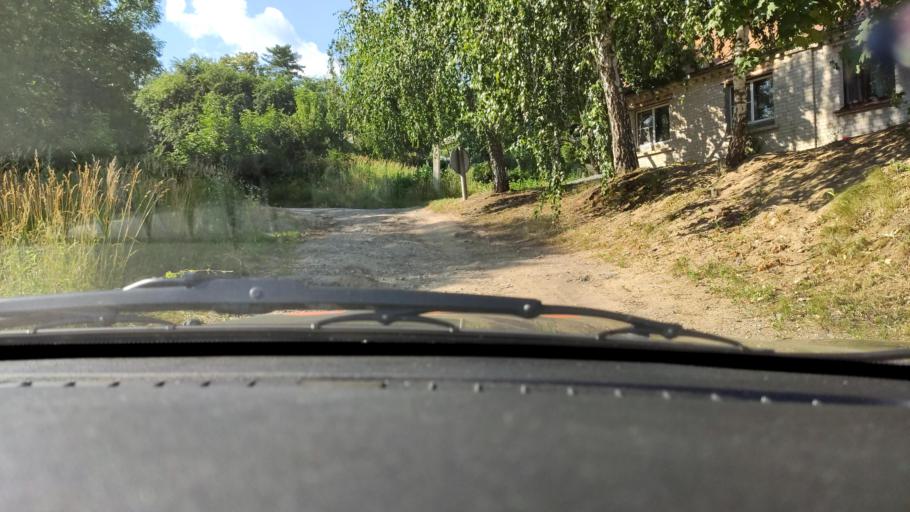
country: RU
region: Voronezj
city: Ramon'
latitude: 51.8227
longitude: 39.2701
